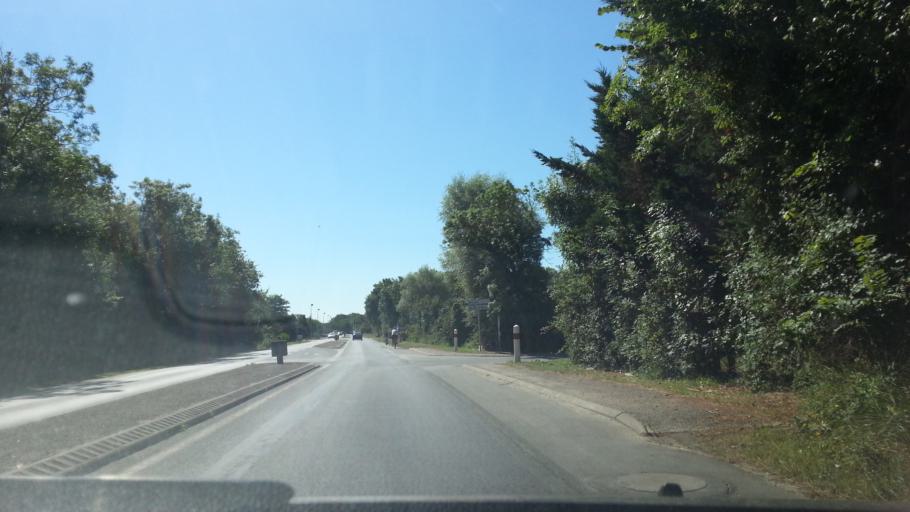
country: FR
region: Poitou-Charentes
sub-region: Departement de la Charente-Maritime
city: Dolus-d'Oleron
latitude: 45.9169
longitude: -1.2747
